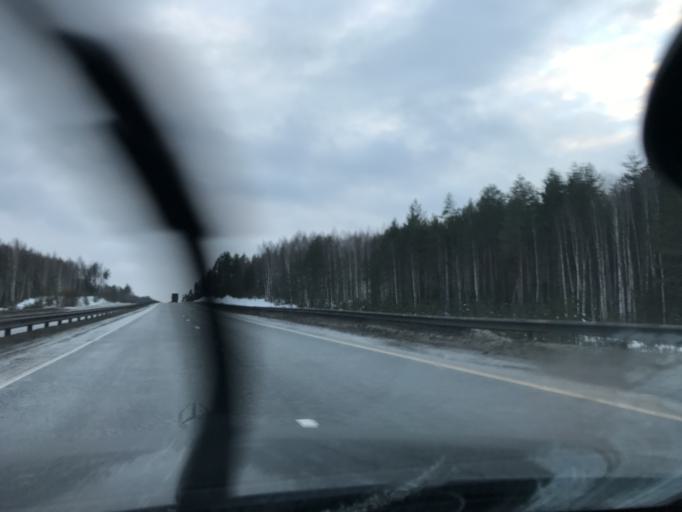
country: RU
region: Vladimir
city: Sudogda
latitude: 56.1223
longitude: 40.8600
